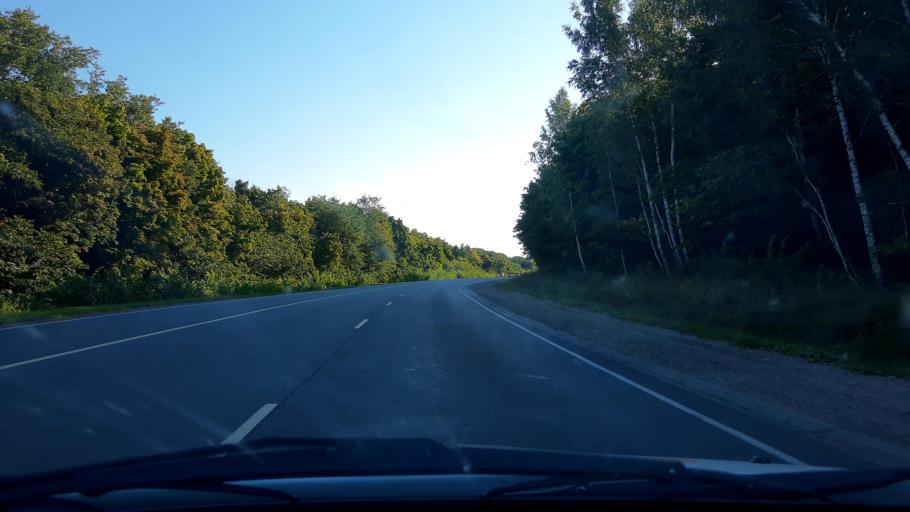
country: RU
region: Bashkortostan
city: Oktyabr'skiy
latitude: 54.4385
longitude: 53.5032
